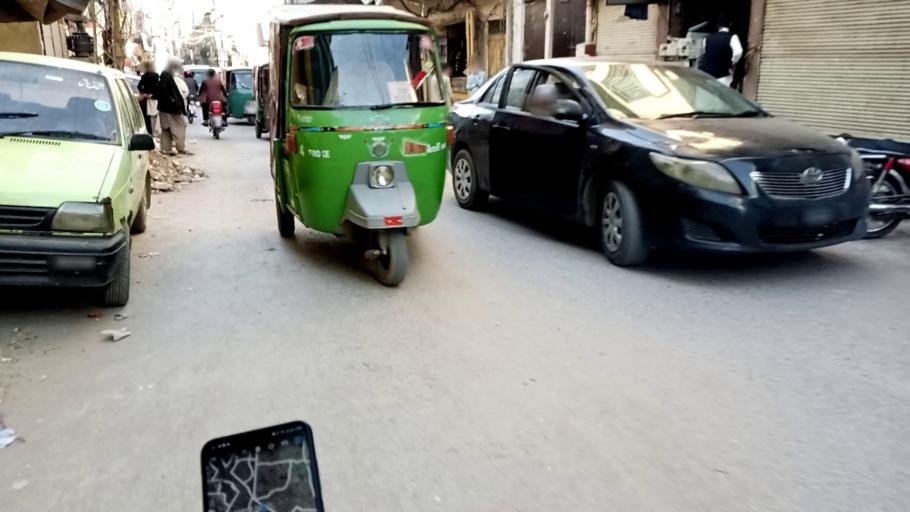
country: PK
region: Khyber Pakhtunkhwa
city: Peshawar
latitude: 34.0032
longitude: 71.5677
